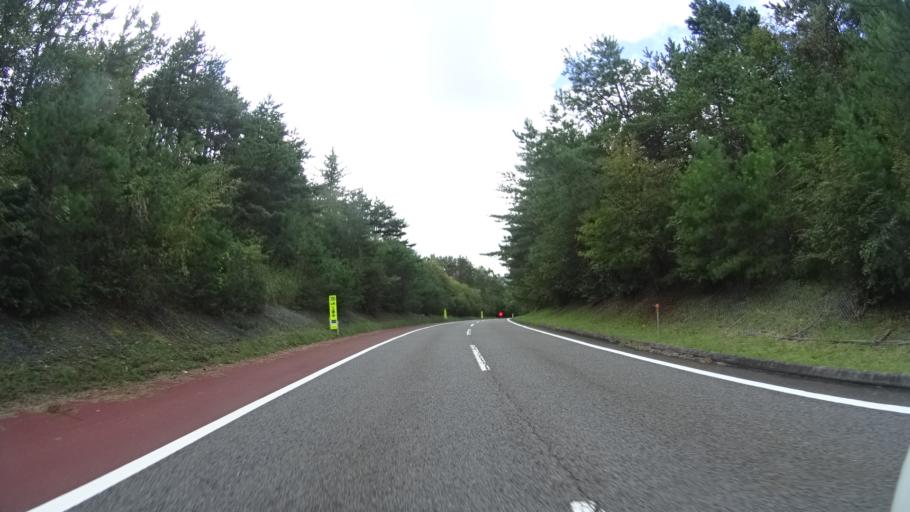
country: JP
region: Oita
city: Tsukawaki
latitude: 33.1344
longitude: 131.2385
